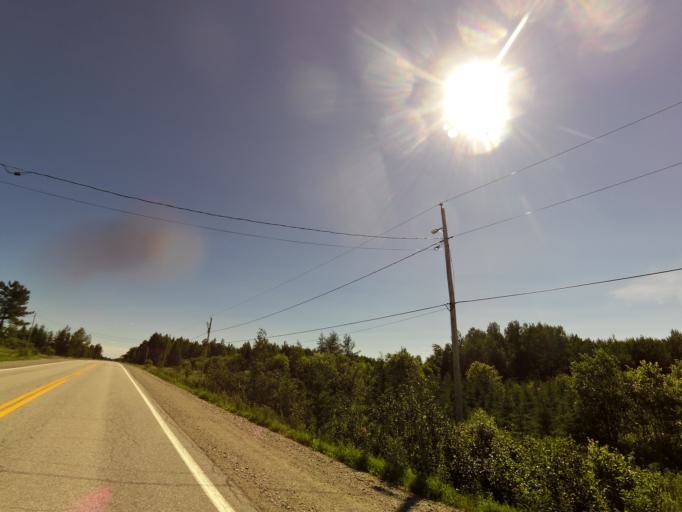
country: CA
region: Quebec
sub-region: Abitibi-Temiscamingue
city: Senneterre
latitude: 48.3031
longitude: -77.3062
